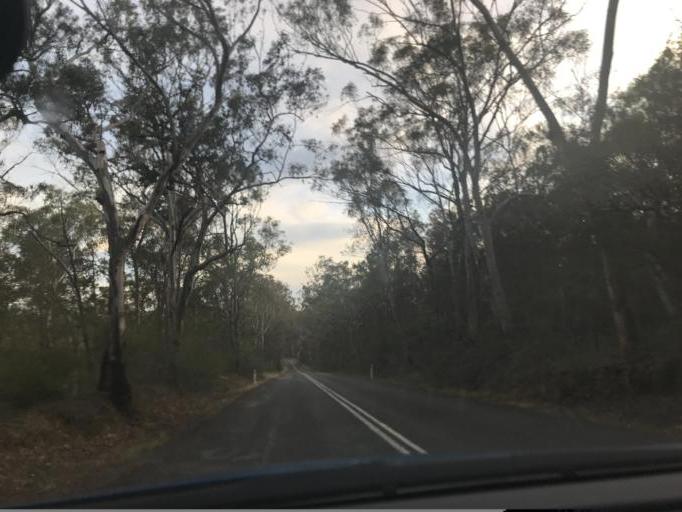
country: AU
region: New South Wales
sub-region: Cessnock
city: Cessnock
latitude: -32.8876
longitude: 151.3002
